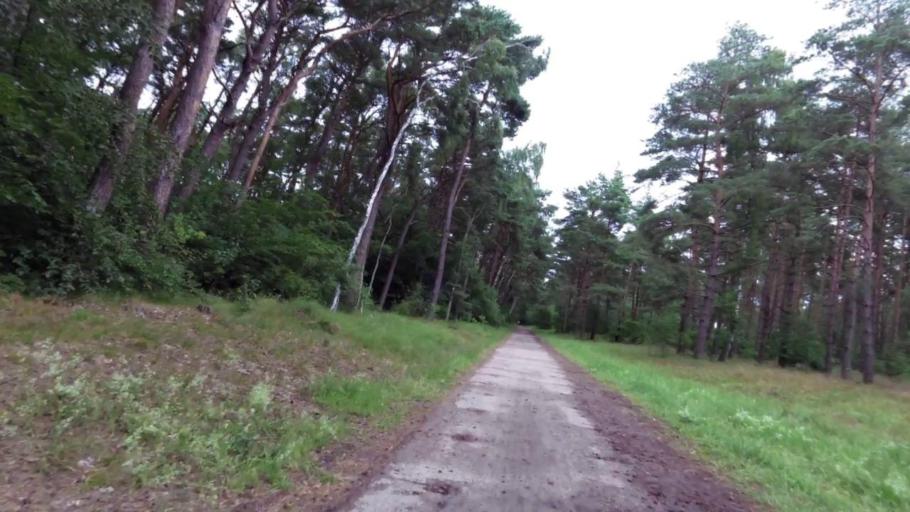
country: PL
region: West Pomeranian Voivodeship
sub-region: Powiat slawienski
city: Darlowo
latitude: 54.5049
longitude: 16.4624
